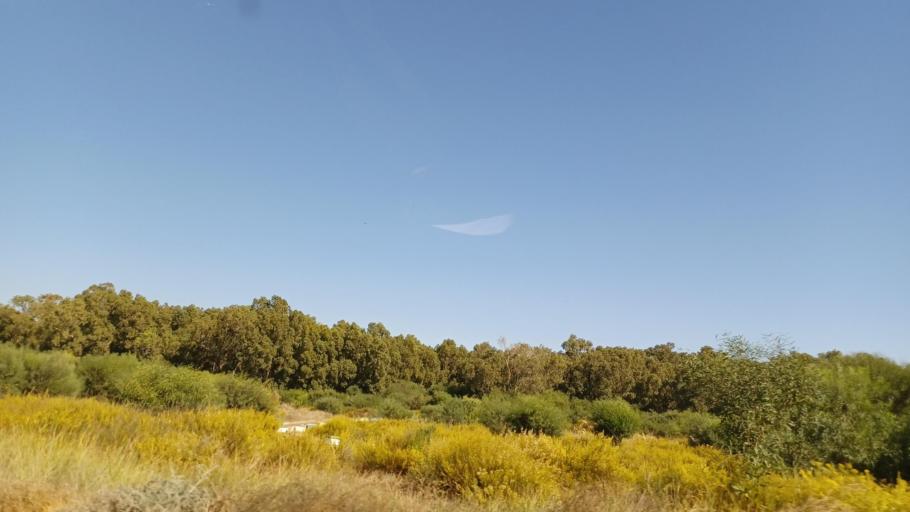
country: CY
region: Larnaka
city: Kolossi
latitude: 34.6239
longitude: 32.9439
